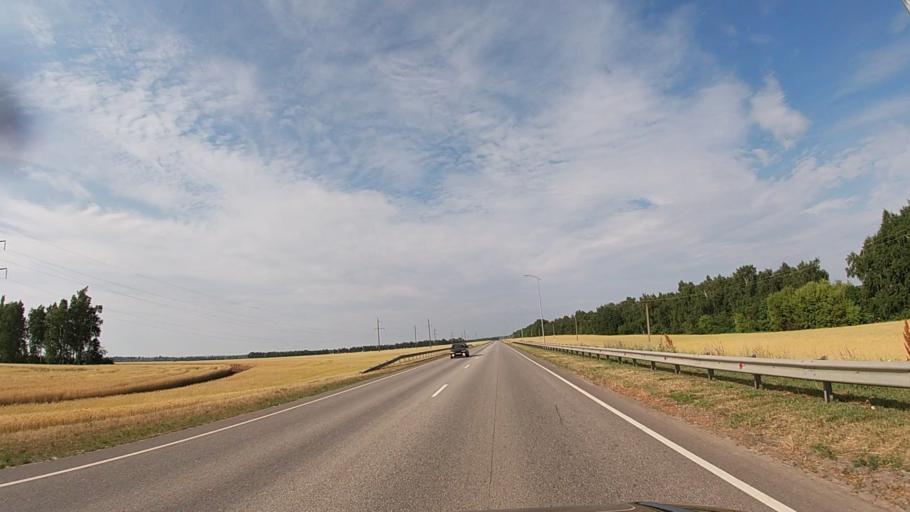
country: RU
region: Belgorod
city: Proletarskiy
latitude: 50.8217
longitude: 35.7578
